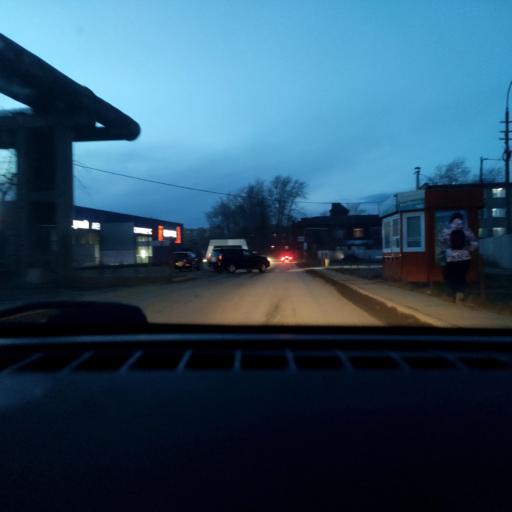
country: RU
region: Perm
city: Froly
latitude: 57.9645
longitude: 56.2721
